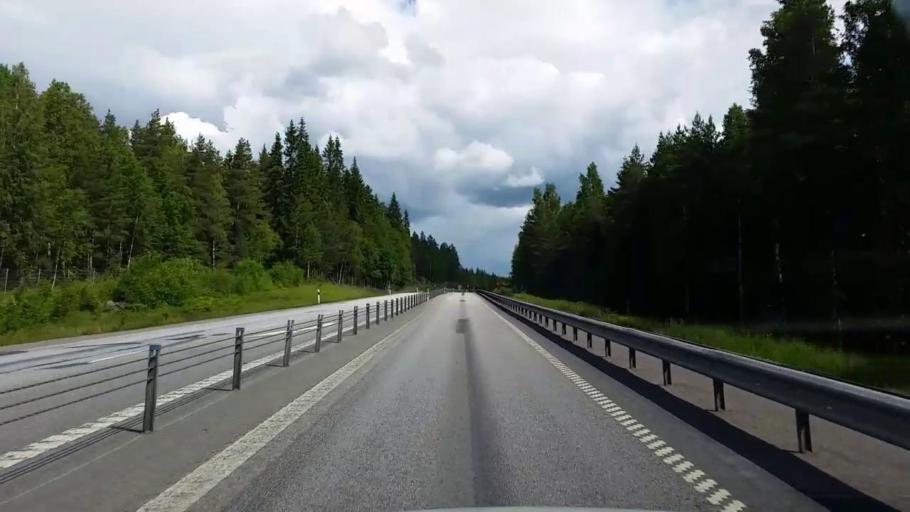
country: SE
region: Vaestmanland
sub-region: Fagersta Kommun
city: Fagersta
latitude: 60.0255
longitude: 15.7976
